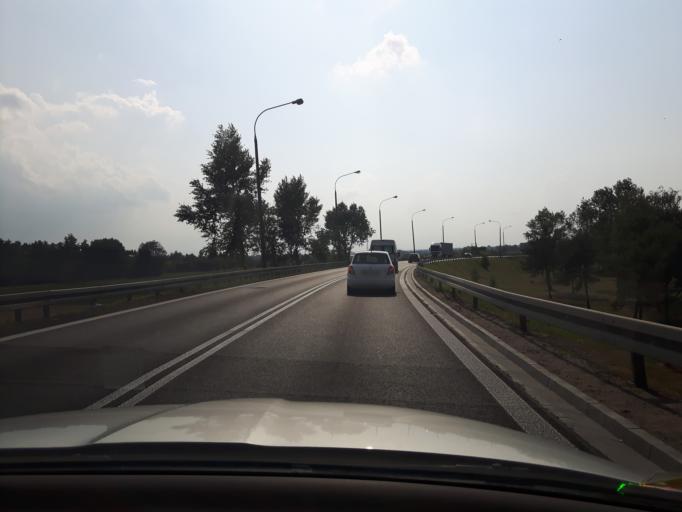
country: PL
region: Masovian Voivodeship
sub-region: Powiat nowodworski
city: Zakroczym
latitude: 52.4400
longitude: 20.6405
